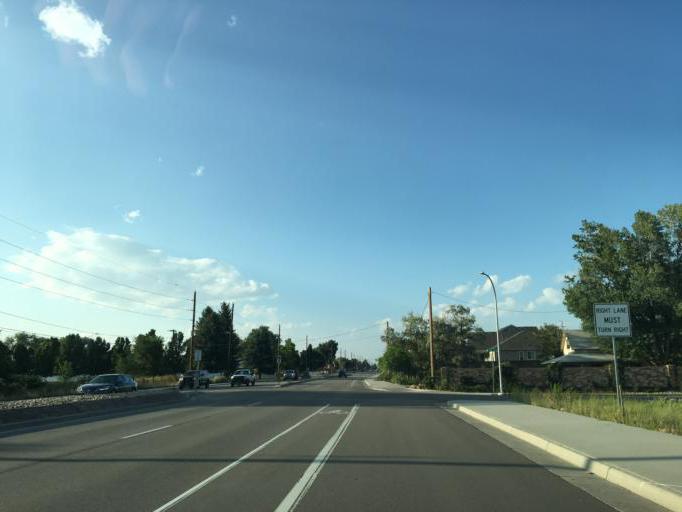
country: US
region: Colorado
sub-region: Jefferson County
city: Applewood
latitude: 39.7880
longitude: -105.1744
